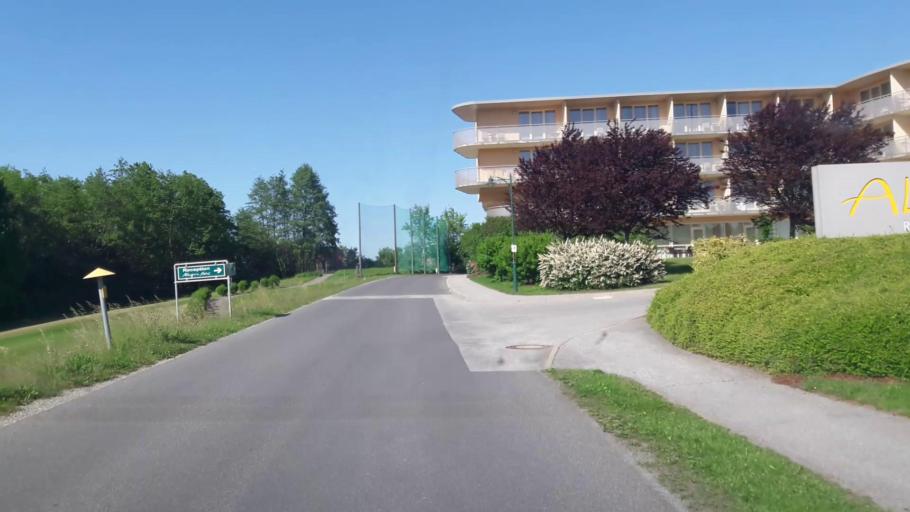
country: AT
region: Burgenland
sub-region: Politischer Bezirk Gussing
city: Stegersbach
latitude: 47.1731
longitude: 16.1473
